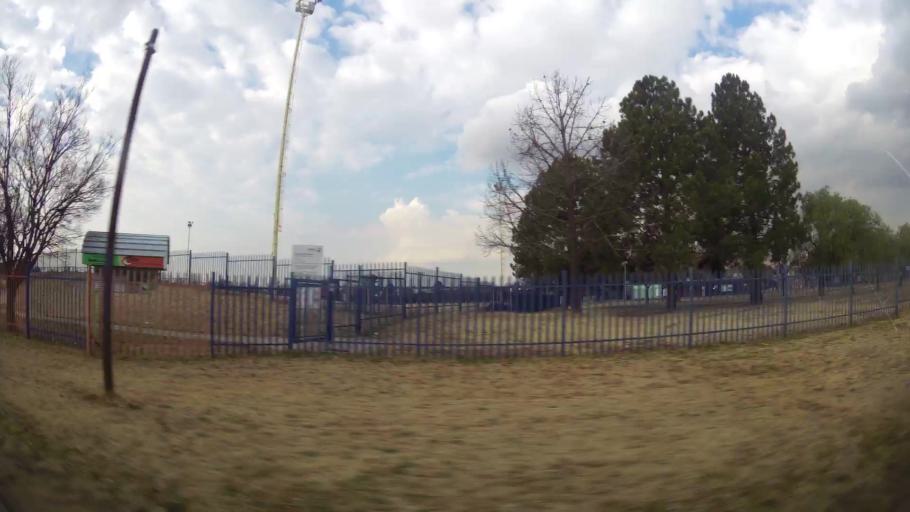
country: ZA
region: Orange Free State
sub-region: Fezile Dabi District Municipality
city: Sasolburg
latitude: -26.7938
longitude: 27.8241
